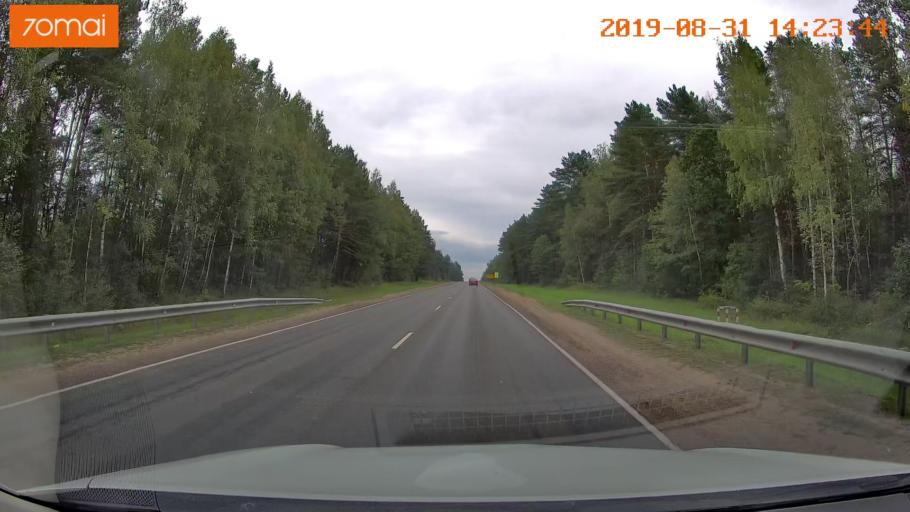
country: RU
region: Smolensk
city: Yekimovichi
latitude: 54.0983
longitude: 33.2400
